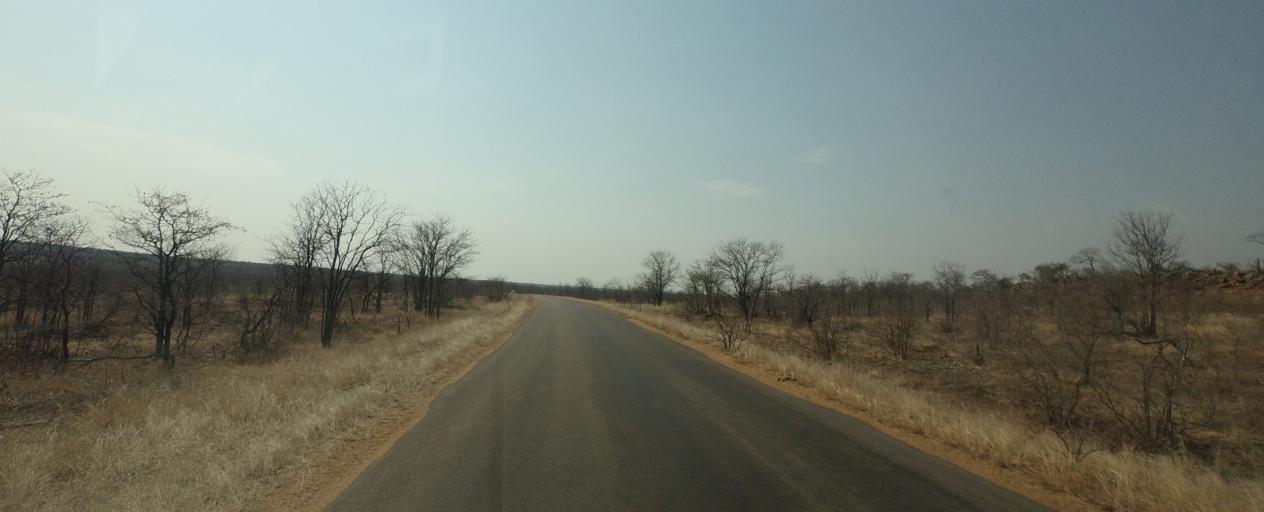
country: ZA
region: Limpopo
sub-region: Mopani District Municipality
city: Phalaborwa
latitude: -23.9547
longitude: 31.6226
